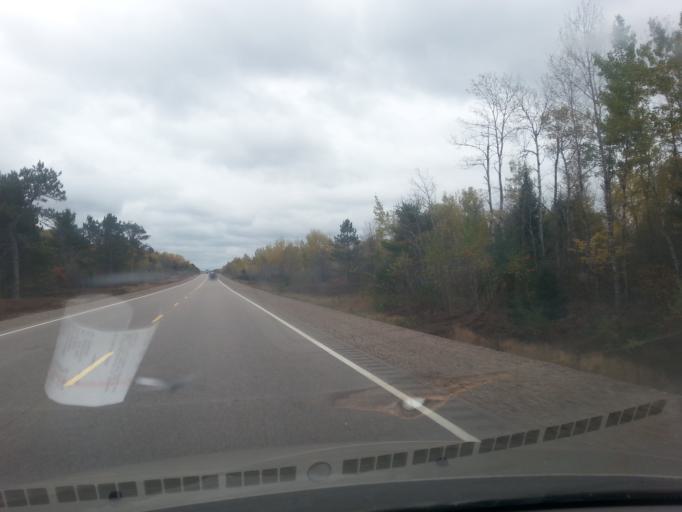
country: CA
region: Ontario
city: Mattawa
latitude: 46.2733
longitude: -78.3679
